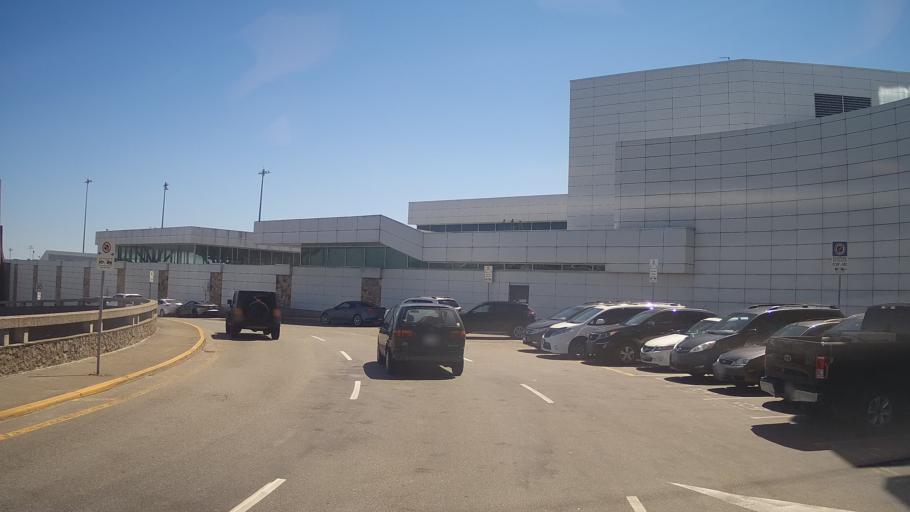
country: CA
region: British Columbia
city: Richmond
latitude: 49.1931
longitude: -123.1808
